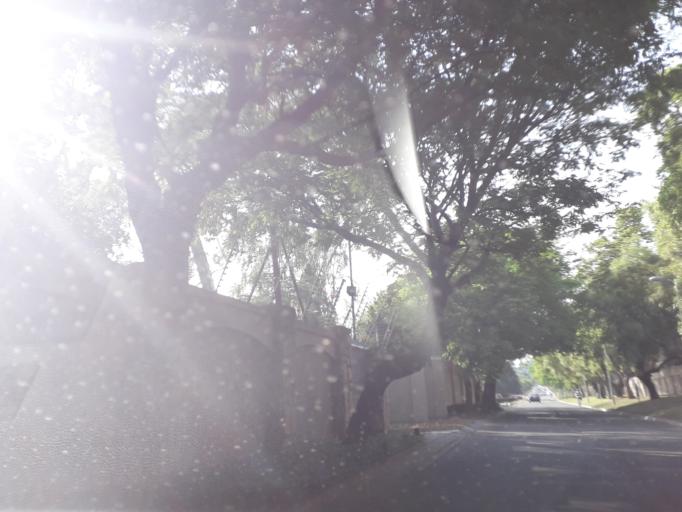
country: ZA
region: Gauteng
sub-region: City of Johannesburg Metropolitan Municipality
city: Diepsloot
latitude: -26.0293
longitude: 28.0138
